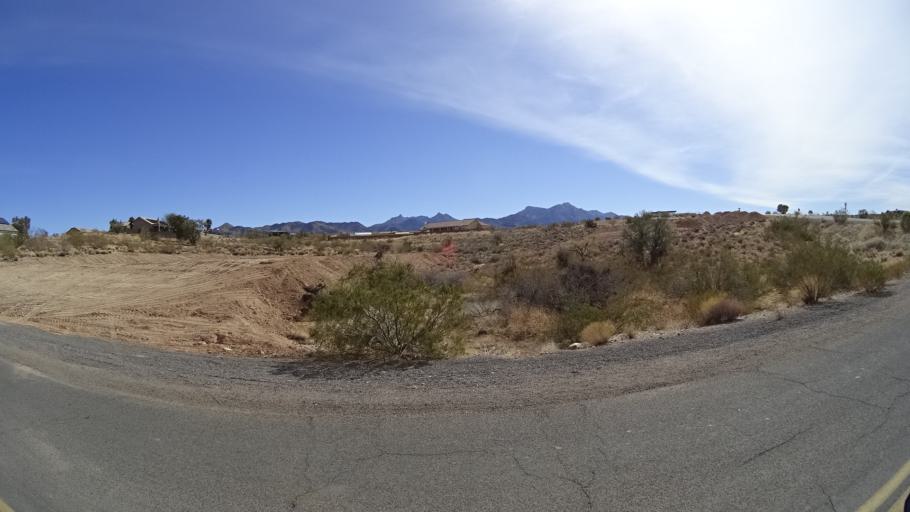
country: US
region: Arizona
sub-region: Mohave County
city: Kingman
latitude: 35.1783
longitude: -114.0011
